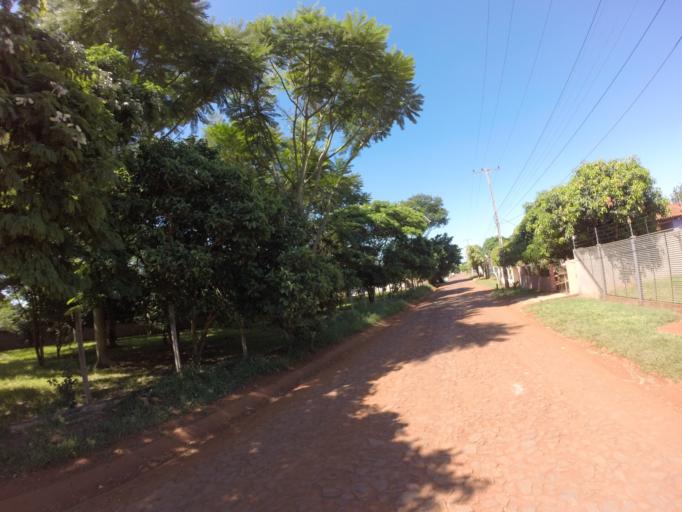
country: PY
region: Alto Parana
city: Ciudad del Este
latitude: -25.4311
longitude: -54.6444
